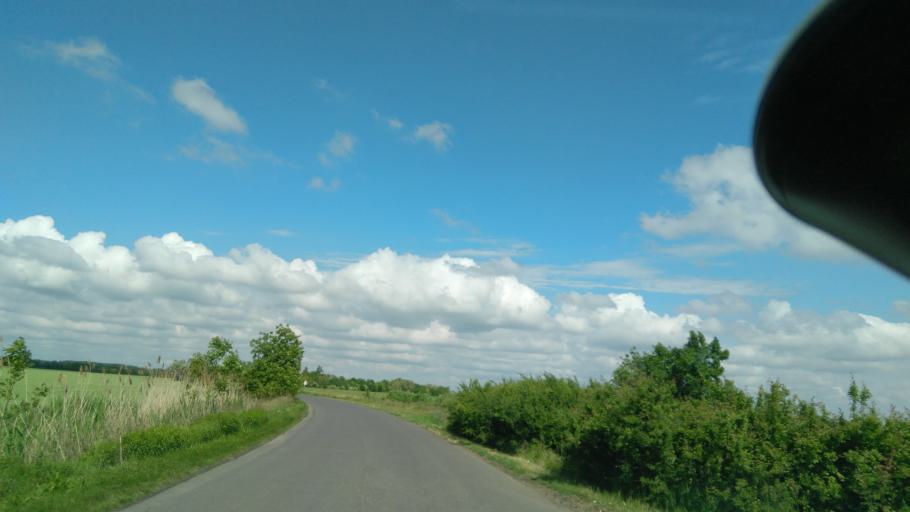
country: HU
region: Bekes
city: Bekes
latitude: 46.8192
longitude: 21.1471
